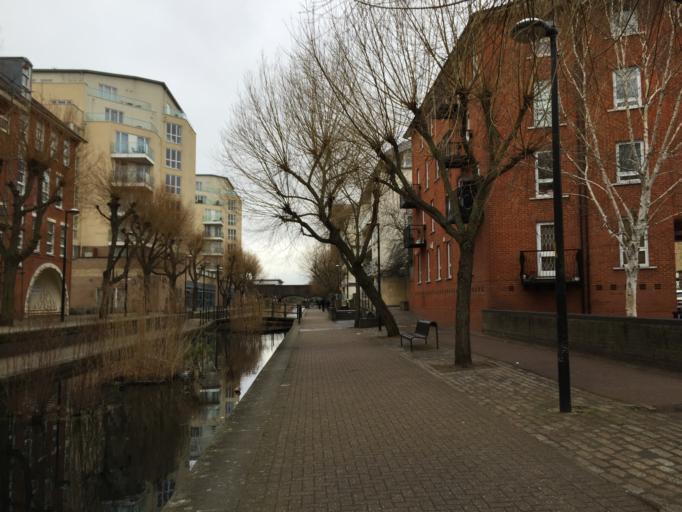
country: GB
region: England
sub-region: Greater London
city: Bethnal Green
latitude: 51.4998
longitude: -0.0460
